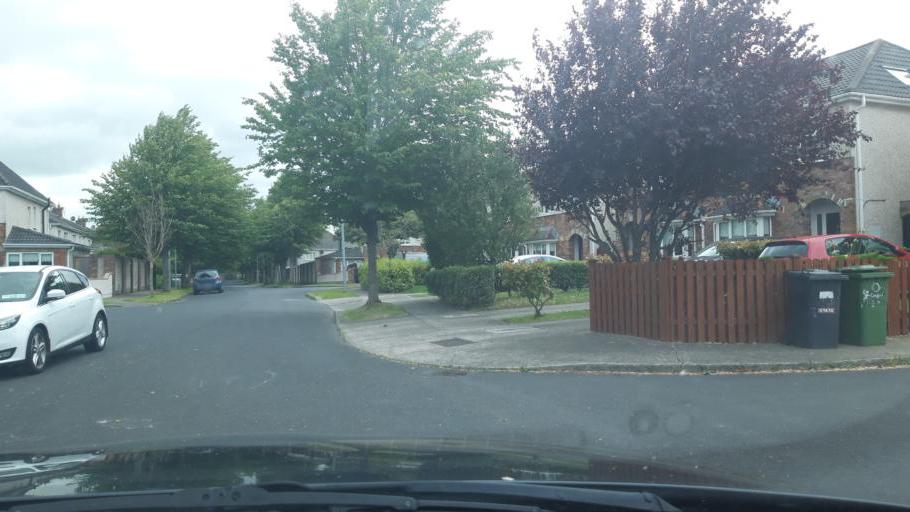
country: IE
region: Leinster
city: Hartstown
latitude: 53.4027
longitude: -6.4220
